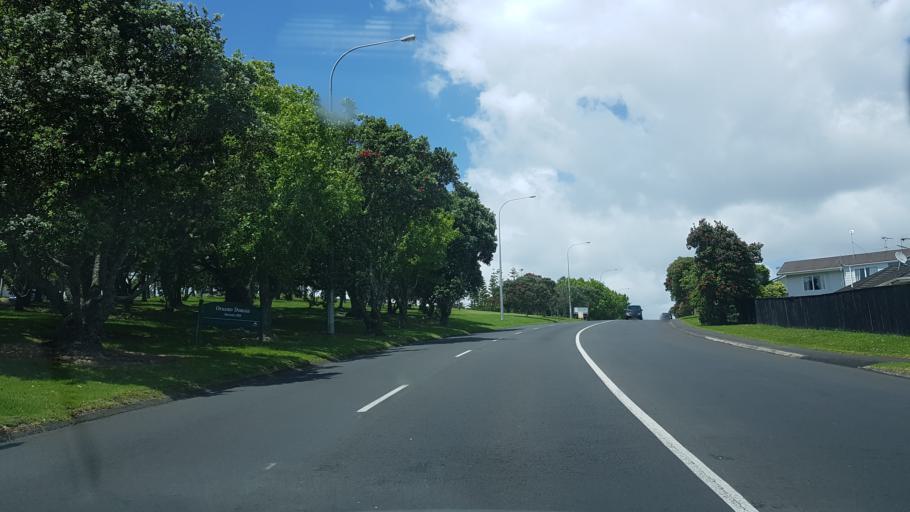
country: NZ
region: Auckland
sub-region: Auckland
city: North Shore
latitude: -36.7848
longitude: 174.7219
